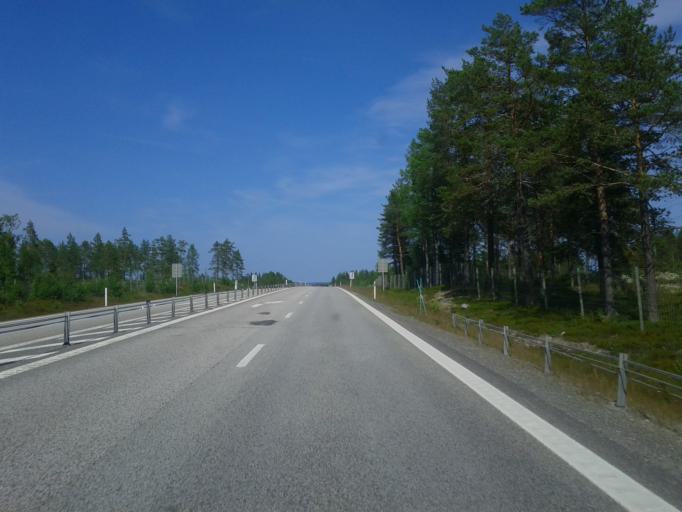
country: SE
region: Vaesterbotten
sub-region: Umea Kommun
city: Hoernefors
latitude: 63.6507
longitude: 19.9475
